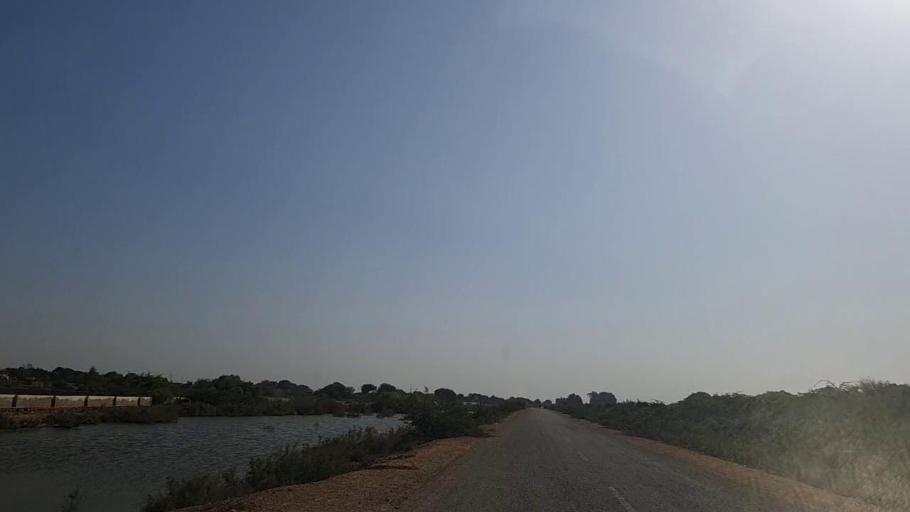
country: PK
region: Sindh
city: Jati
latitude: 24.4302
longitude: 68.2589
